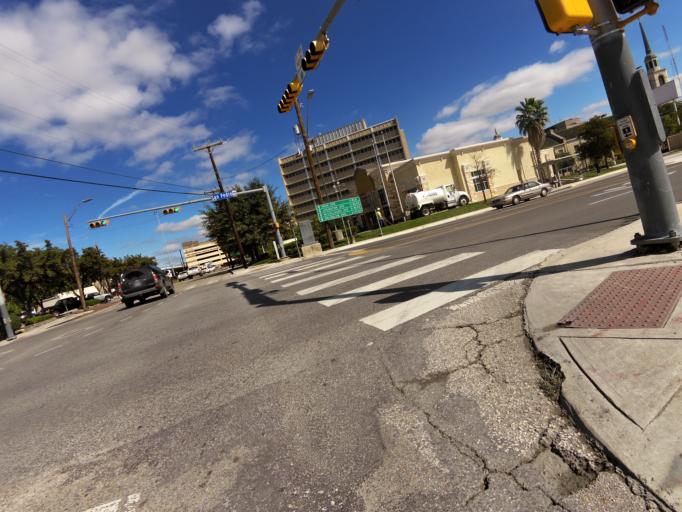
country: US
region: Texas
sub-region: Bexar County
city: San Antonio
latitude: 29.4345
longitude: -98.4952
